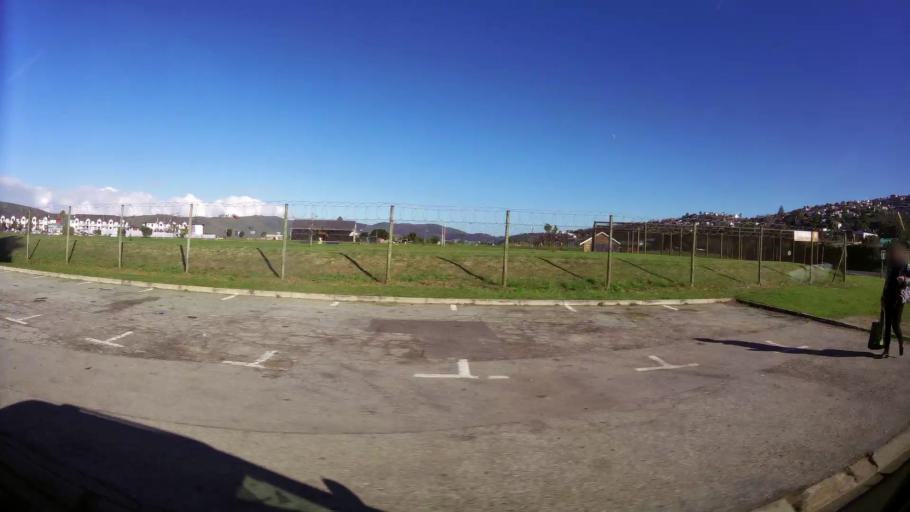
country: ZA
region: Western Cape
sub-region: Eden District Municipality
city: Knysna
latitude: -34.0380
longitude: 23.0436
